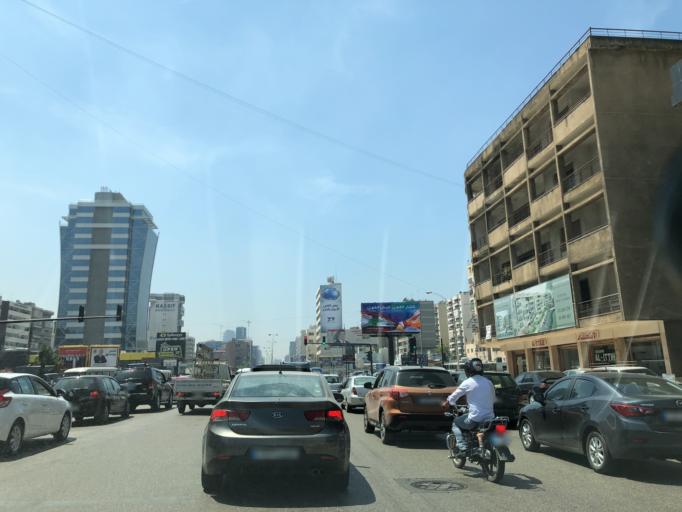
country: LB
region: Mont-Liban
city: Jdaidet el Matn
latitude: 33.8926
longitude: 35.5592
